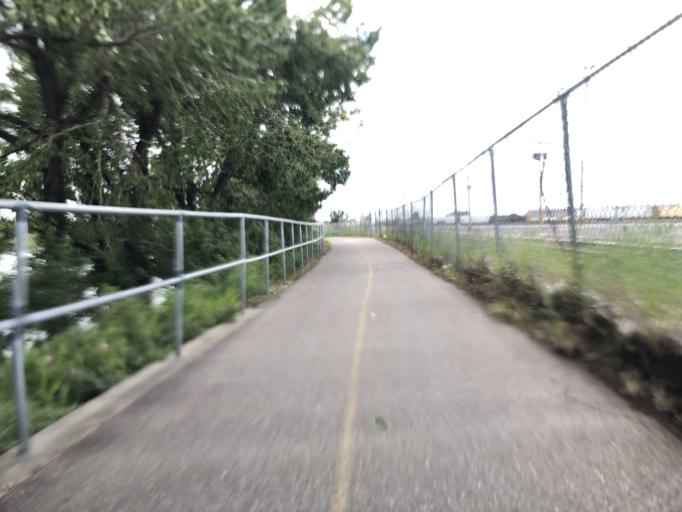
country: CA
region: Alberta
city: Calgary
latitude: 51.0207
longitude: -114.0127
